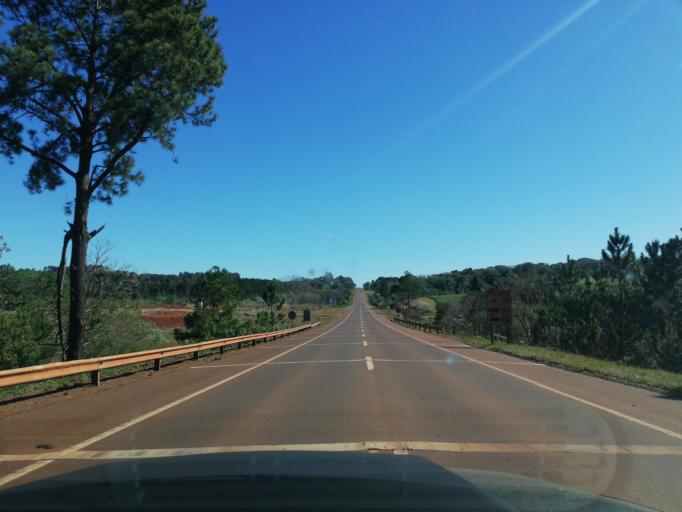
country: AR
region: Misiones
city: Aristobulo del Valle
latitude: -27.0856
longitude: -54.8430
